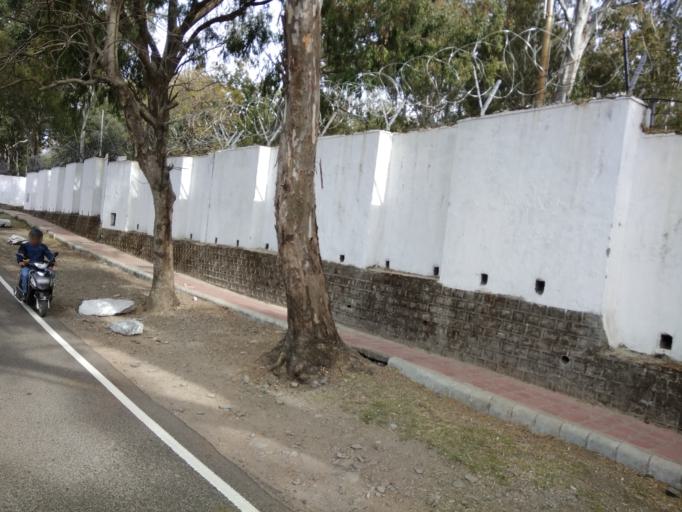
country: IN
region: Himachal Pradesh
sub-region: Kangra
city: Dharmsala
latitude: 32.1797
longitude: 76.3779
